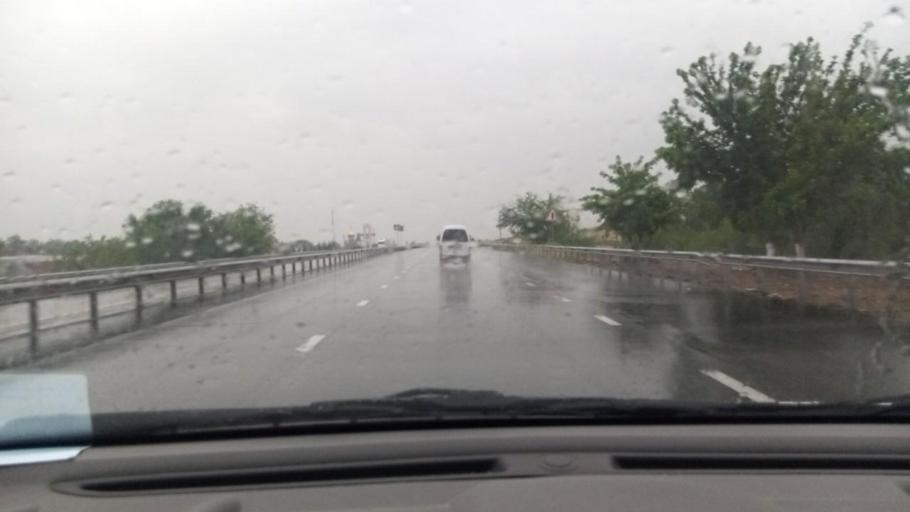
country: UZ
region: Toshkent
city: Tuytepa
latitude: 41.1245
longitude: 69.4389
